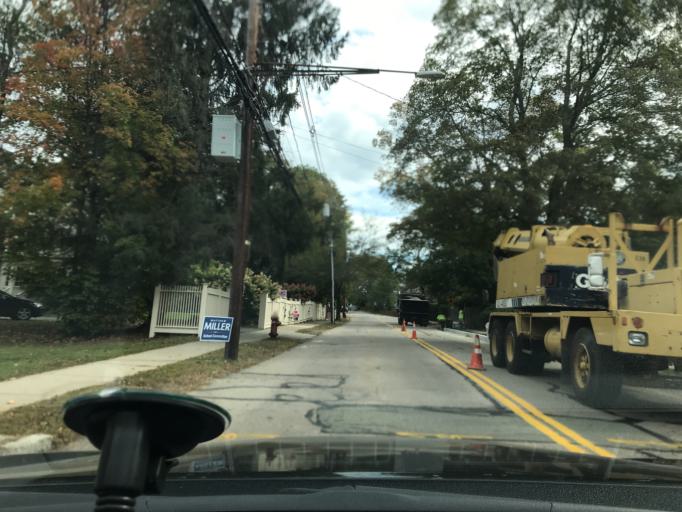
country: US
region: Massachusetts
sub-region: Middlesex County
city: Newton
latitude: 42.3386
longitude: -71.1798
